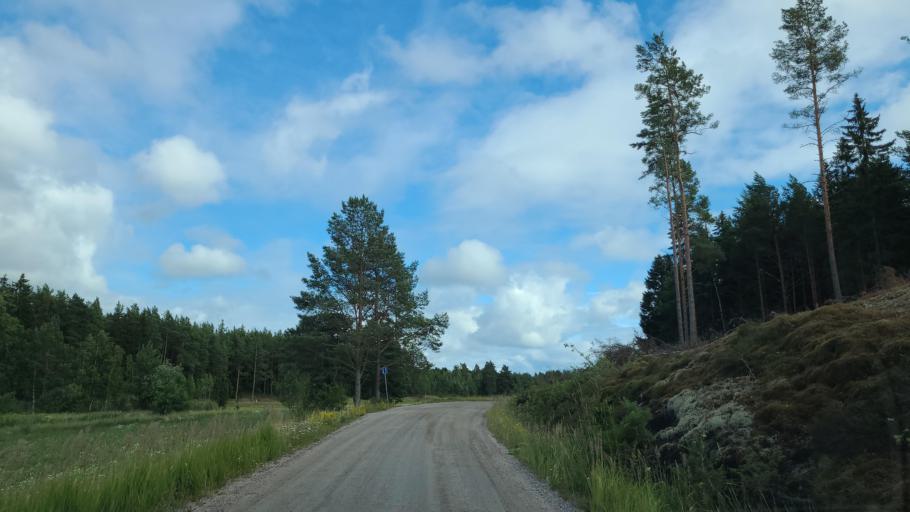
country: FI
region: Varsinais-Suomi
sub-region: Aboland-Turunmaa
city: Nagu
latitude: 60.1498
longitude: 21.7739
